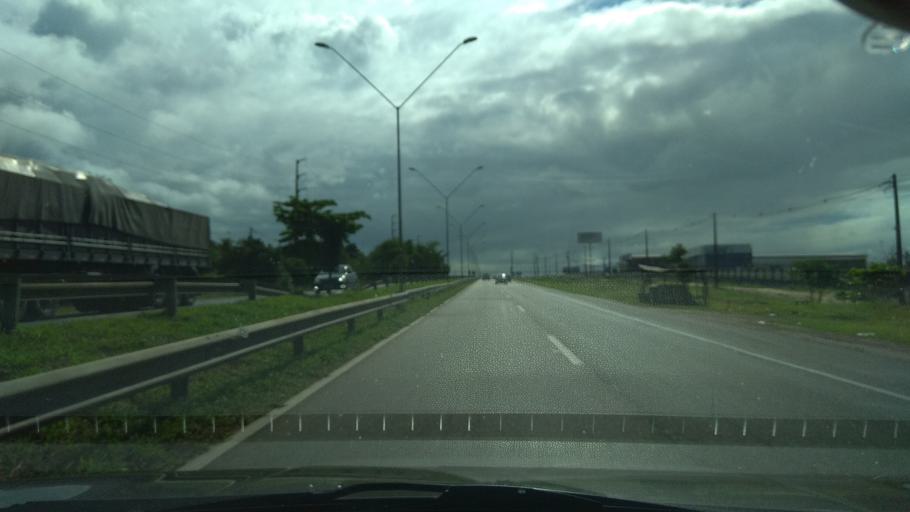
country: BR
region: Bahia
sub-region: Conceicao Do Jacuipe
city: Conceicao do Jacuipe
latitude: -12.3226
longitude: -38.8690
